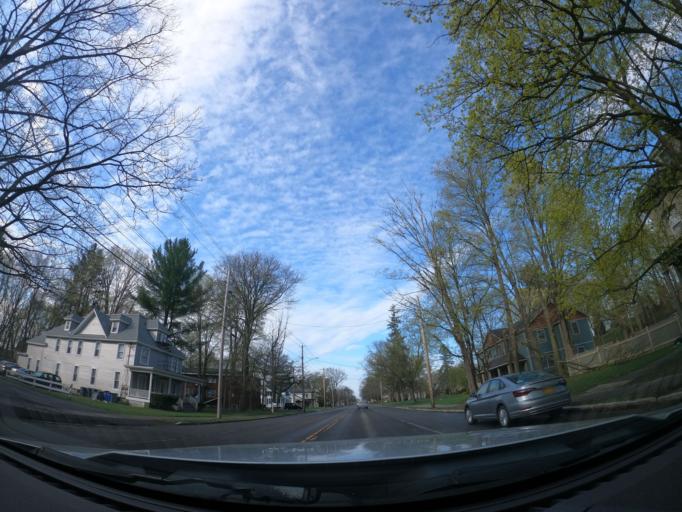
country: US
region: New York
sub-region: Cortland County
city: Cortland
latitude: 42.5940
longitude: -76.1861
